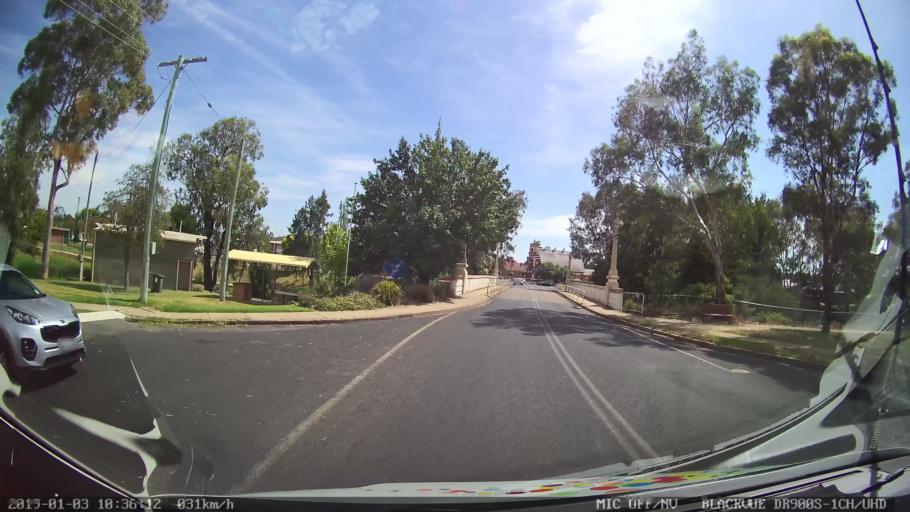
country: AU
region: New South Wales
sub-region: Young
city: Young
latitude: -34.3163
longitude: 148.2968
